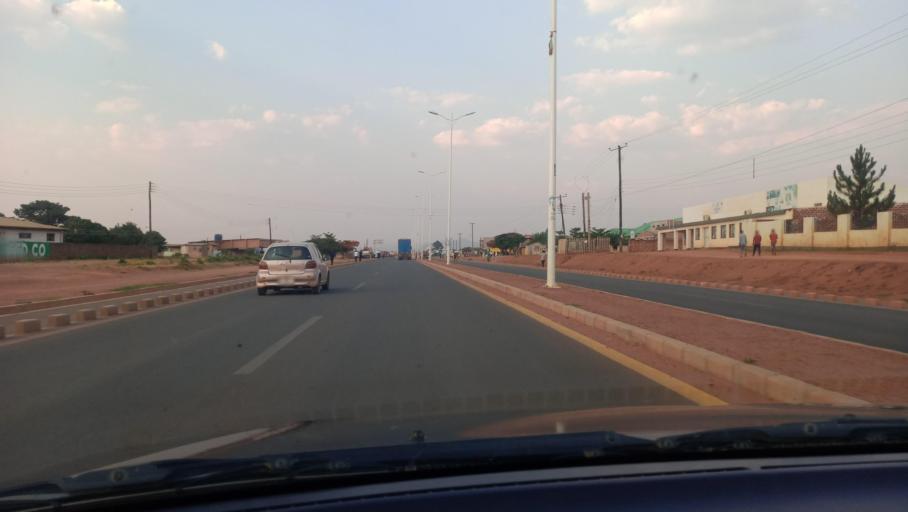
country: ZM
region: Northern
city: Mpika
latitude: -11.8396
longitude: 31.4453
